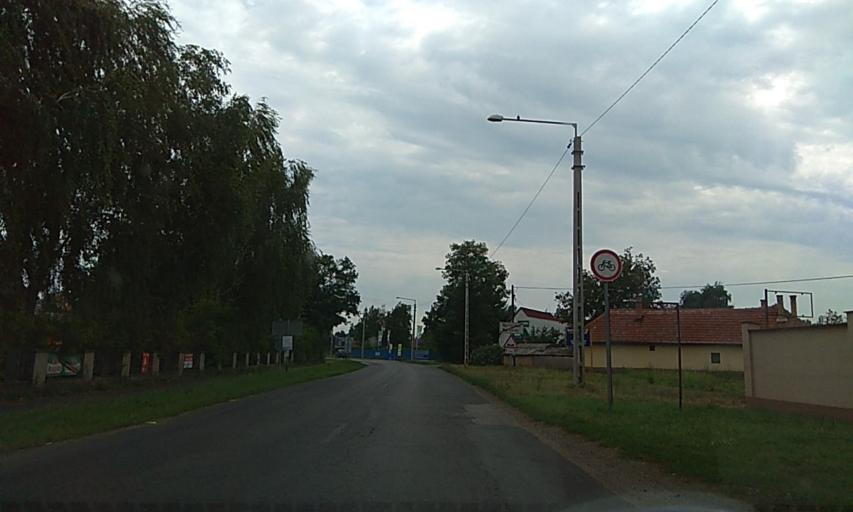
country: HU
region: Szabolcs-Szatmar-Bereg
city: Kotaj
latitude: 48.0133
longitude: 21.6887
